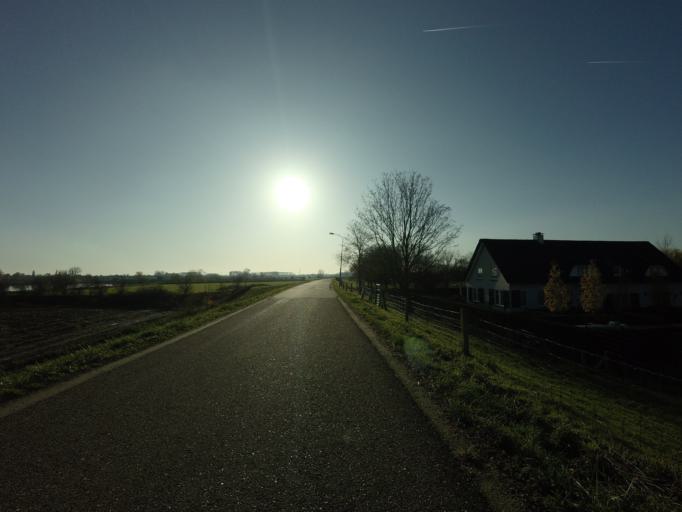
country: NL
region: North Brabant
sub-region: Gemeente 's-Hertogenbosch
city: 's-Hertogenbosch
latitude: 51.7590
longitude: 5.3417
